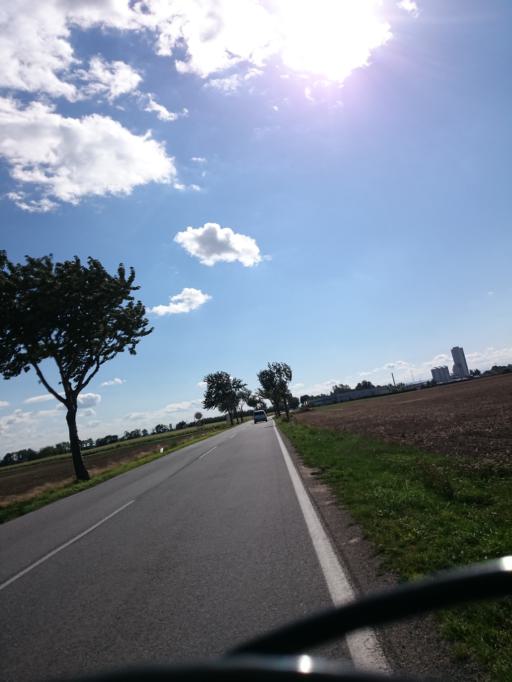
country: AT
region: Lower Austria
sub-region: Politischer Bezirk Ganserndorf
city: Grosshofen
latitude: 48.2442
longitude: 16.5965
